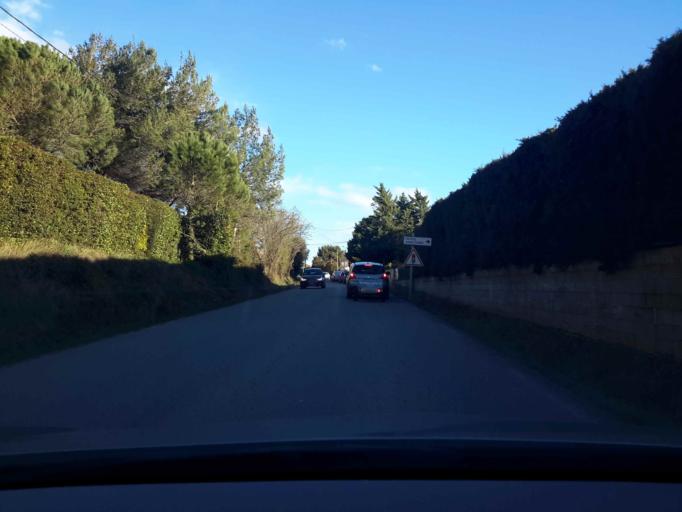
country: FR
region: Languedoc-Roussillon
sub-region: Departement du Gard
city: Generac
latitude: 43.7360
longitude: 4.3453
